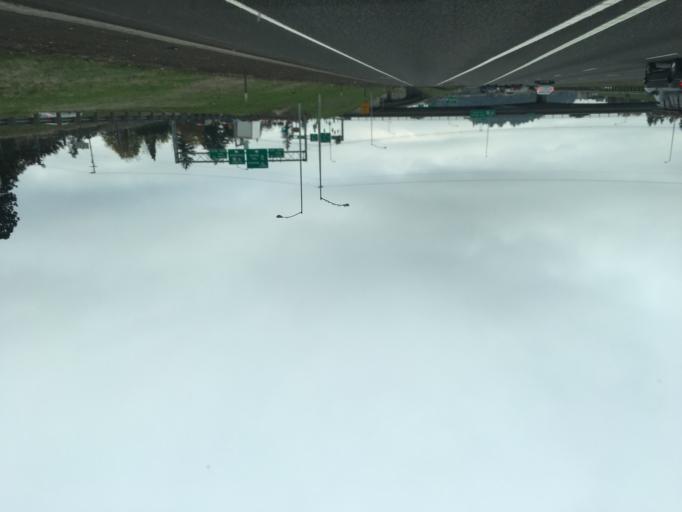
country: US
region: Oregon
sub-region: Multnomah County
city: Lents
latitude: 45.5244
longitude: -122.5651
